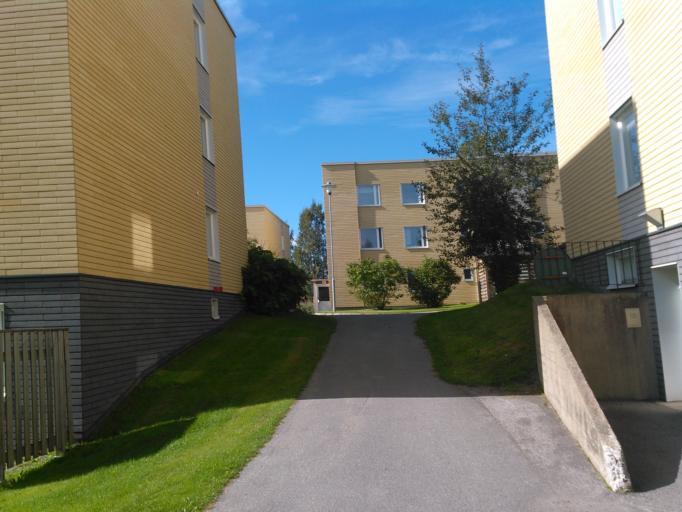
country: SE
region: Vaesterbotten
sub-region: Umea Kommun
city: Umea
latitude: 63.8000
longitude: 20.3249
